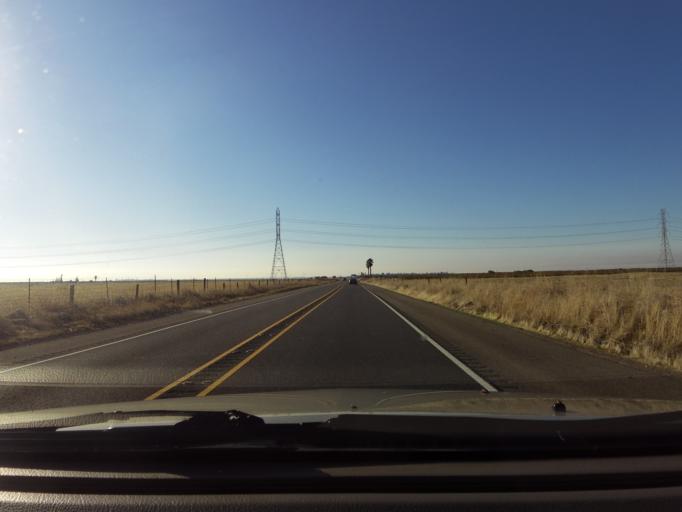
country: US
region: California
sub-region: Madera County
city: Bonadelle Ranchos-Madera Ranchos
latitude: 36.9460
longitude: -119.7940
